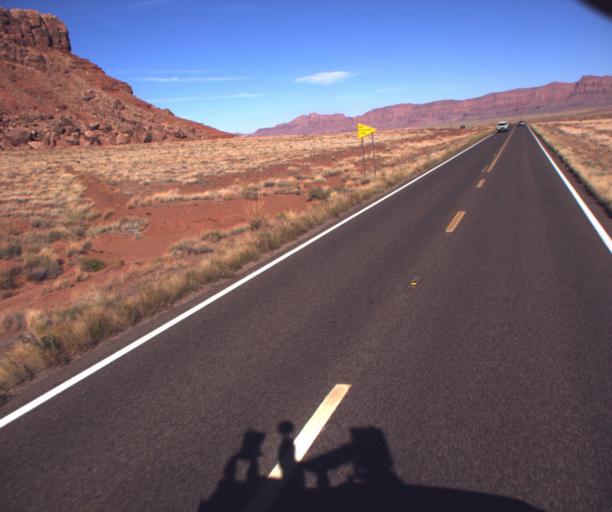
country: US
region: Arizona
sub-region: Coconino County
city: Page
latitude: 36.7523
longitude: -111.7227
